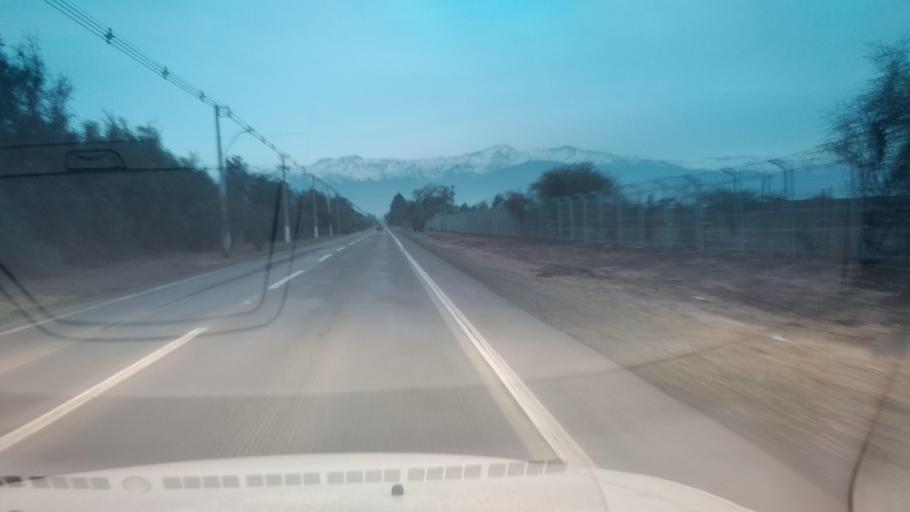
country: CL
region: Santiago Metropolitan
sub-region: Provincia de Chacabuco
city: Chicureo Abajo
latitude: -33.0932
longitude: -70.7155
